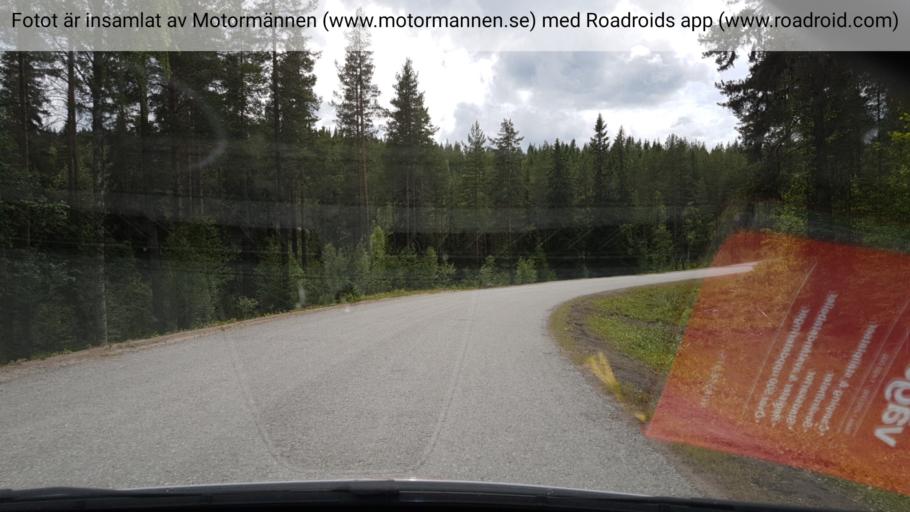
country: SE
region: Vaesternorrland
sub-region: Solleftea Kommun
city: Solleftea
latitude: 63.3845
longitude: 17.5024
